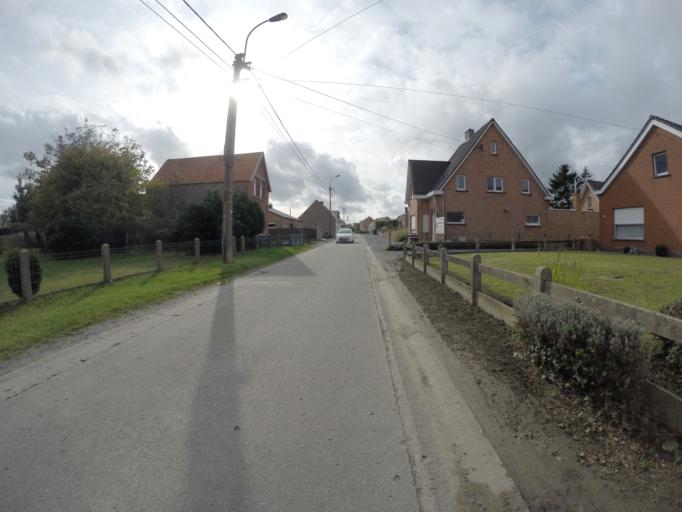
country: BE
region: Flanders
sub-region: Provincie West-Vlaanderen
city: Beernem
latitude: 51.0959
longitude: 3.3712
